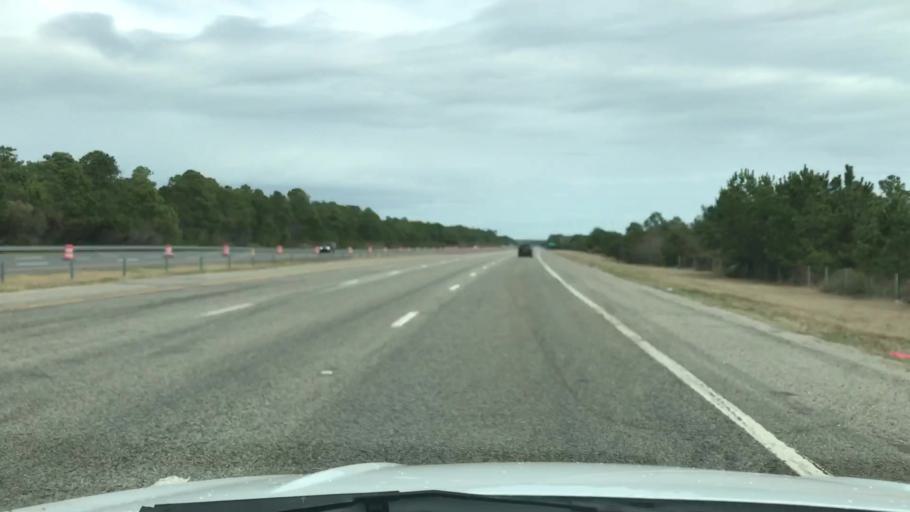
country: US
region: South Carolina
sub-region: Horry County
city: Socastee
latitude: 33.7117
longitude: -79.0067
